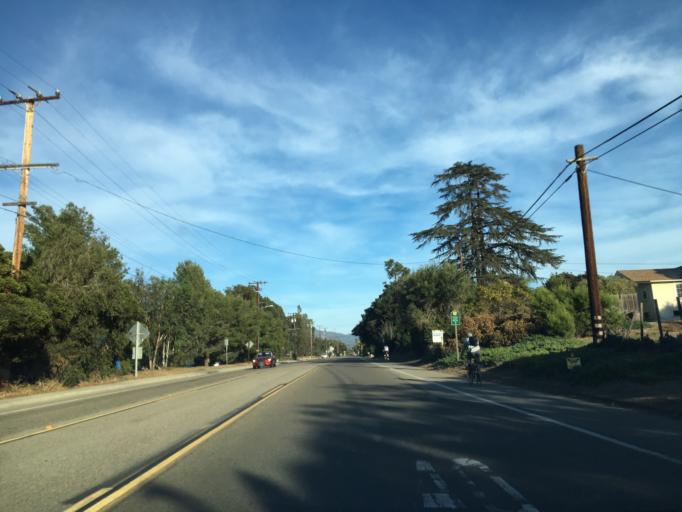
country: US
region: California
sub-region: Santa Barbara County
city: Goleta
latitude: 34.4385
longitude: -119.7792
